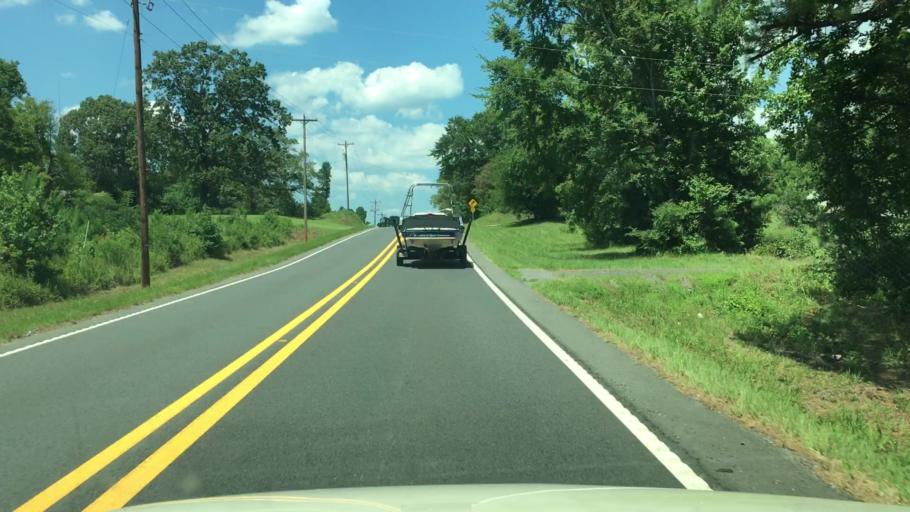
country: US
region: Arkansas
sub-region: Garland County
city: Lake Hamilton
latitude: 34.2884
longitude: -93.1635
